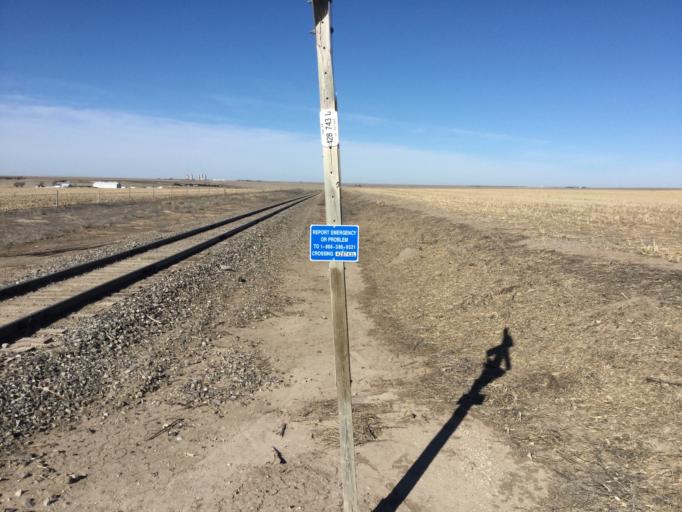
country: US
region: Kansas
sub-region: Wichita County
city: Leoti
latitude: 38.4849
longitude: -101.4763
